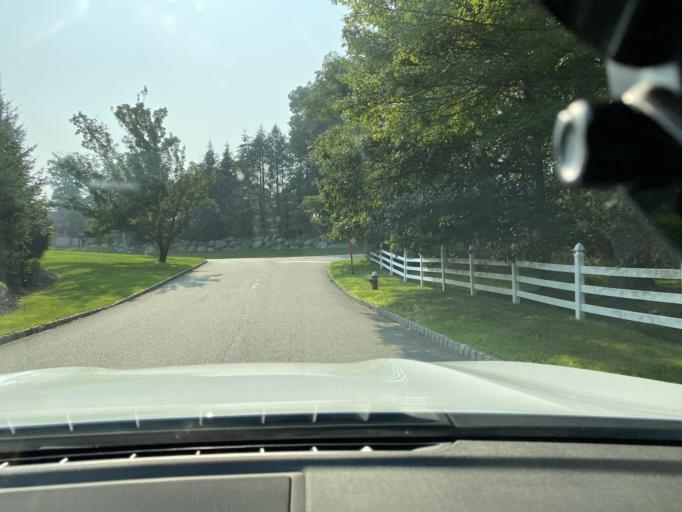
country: US
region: New York
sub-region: Rockland County
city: Airmont
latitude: 41.0883
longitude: -74.1140
